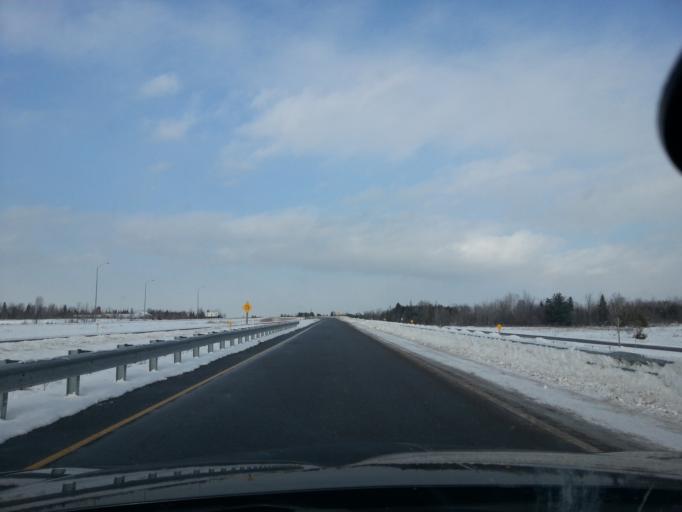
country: CA
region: Ontario
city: Carleton Place
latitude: 45.1731
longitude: -76.0479
